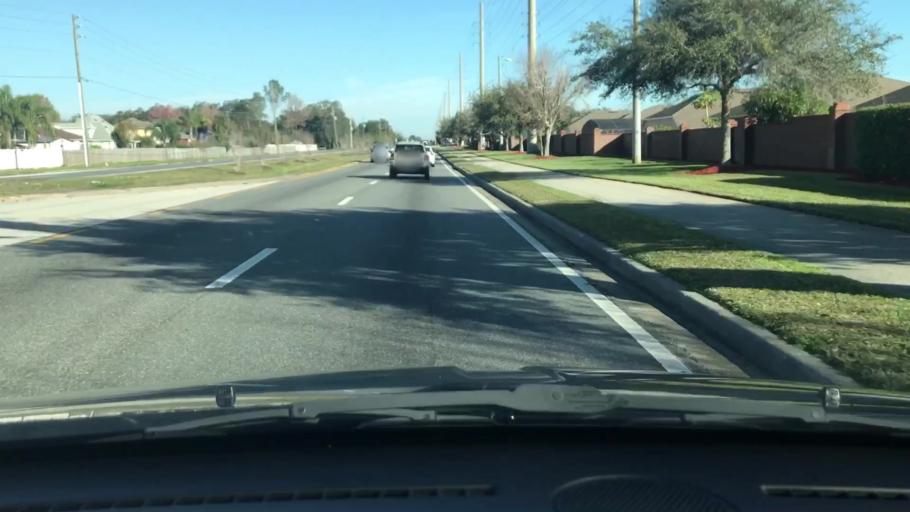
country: US
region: Florida
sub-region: Osceola County
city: Campbell
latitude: 28.2435
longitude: -81.4360
